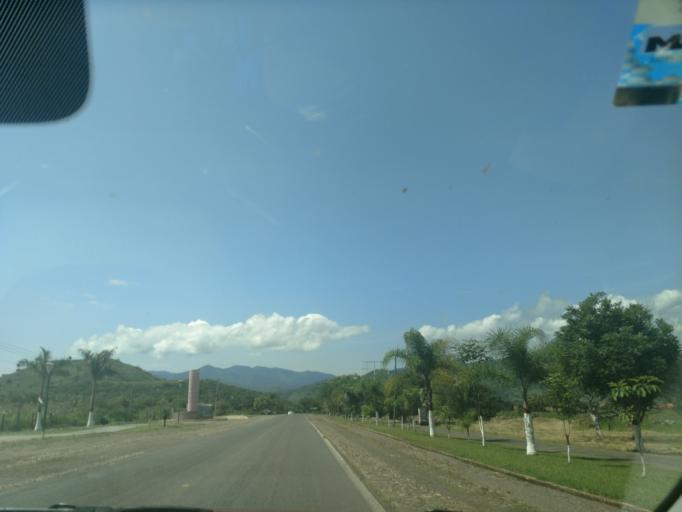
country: MX
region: Jalisco
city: Talpa de Allende
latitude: 20.3966
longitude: -104.8170
